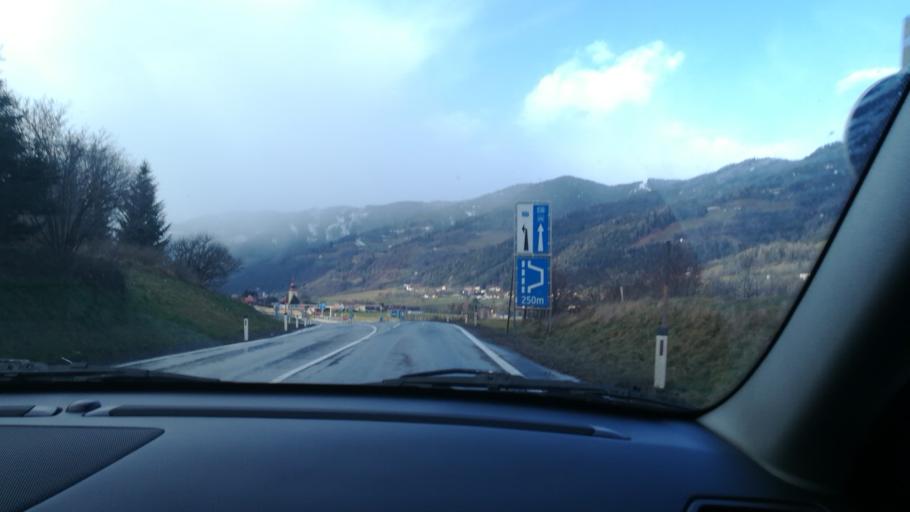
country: AT
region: Styria
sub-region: Politischer Bezirk Murtal
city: Sankt Georgen ob Judenburg
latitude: 47.2031
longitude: 14.5113
